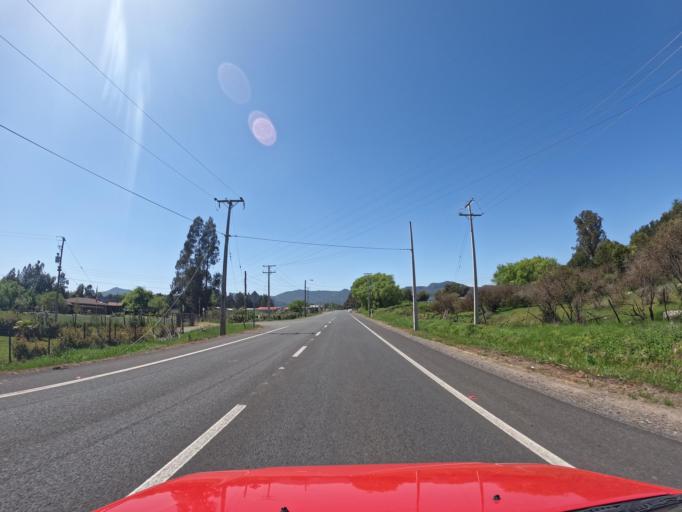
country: CL
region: Maule
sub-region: Provincia de Linares
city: Colbun
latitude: -35.7158
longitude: -71.4055
